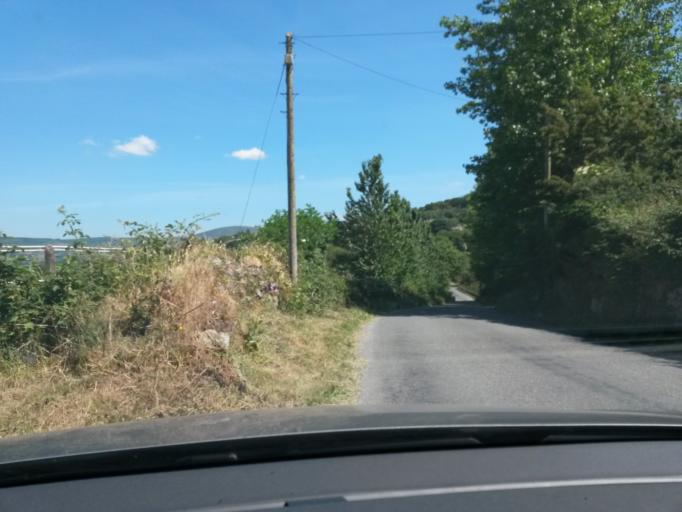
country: IE
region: Leinster
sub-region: Wicklow
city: Valleymount
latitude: 53.0992
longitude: -6.5073
